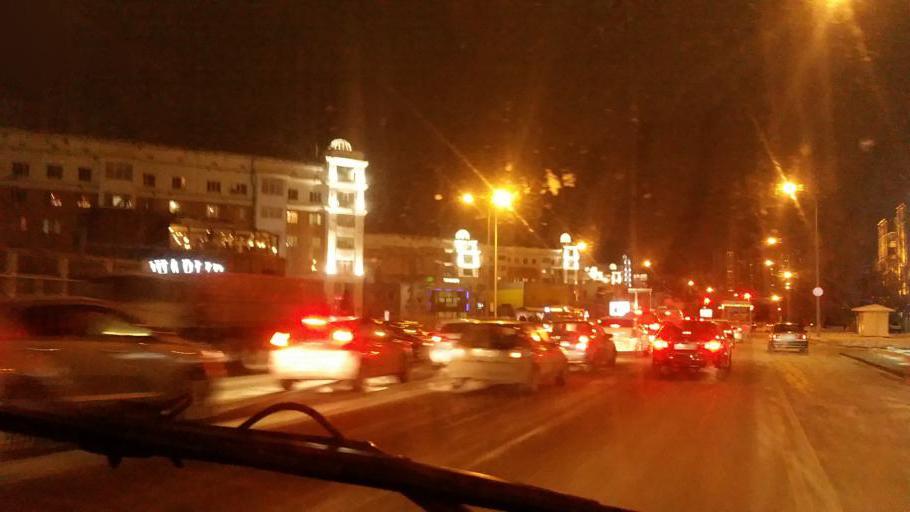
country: KZ
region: Astana Qalasy
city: Astana
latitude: 51.1569
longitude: 71.4355
